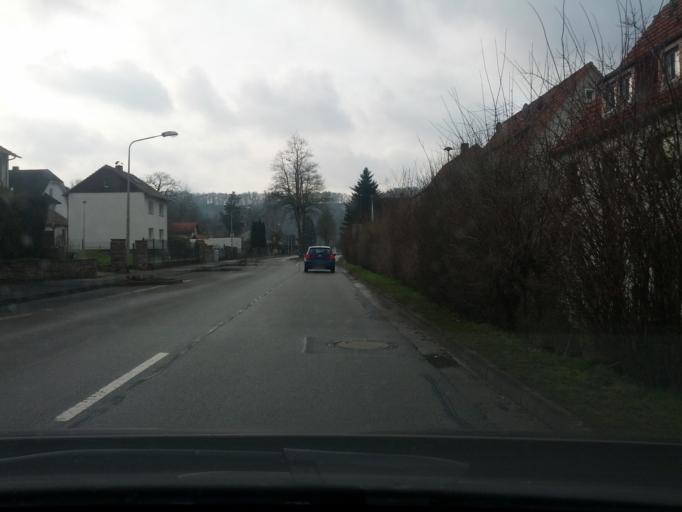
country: DE
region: Lower Saxony
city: Bad Karlshafen
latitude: 51.6482
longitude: 9.4594
